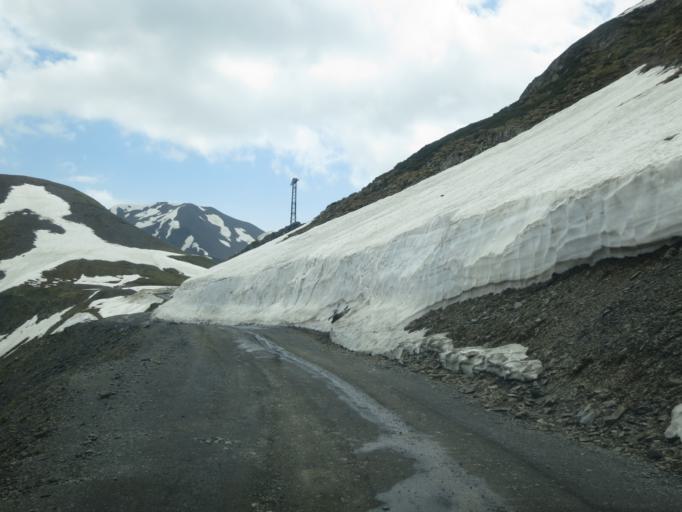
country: GE
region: Kakheti
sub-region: Telavi
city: Telavi
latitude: 42.2799
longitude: 45.5047
